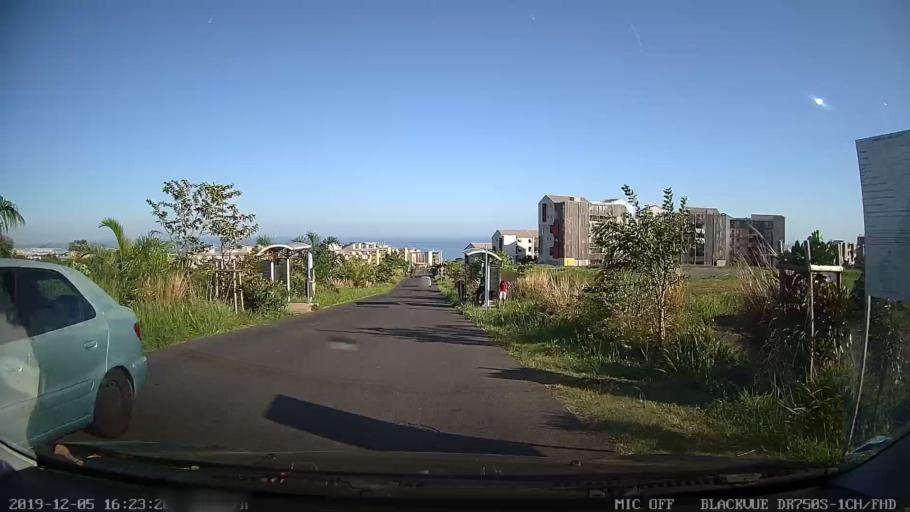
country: RE
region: Reunion
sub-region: Reunion
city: Sainte-Marie
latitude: -20.9205
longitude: 55.5280
